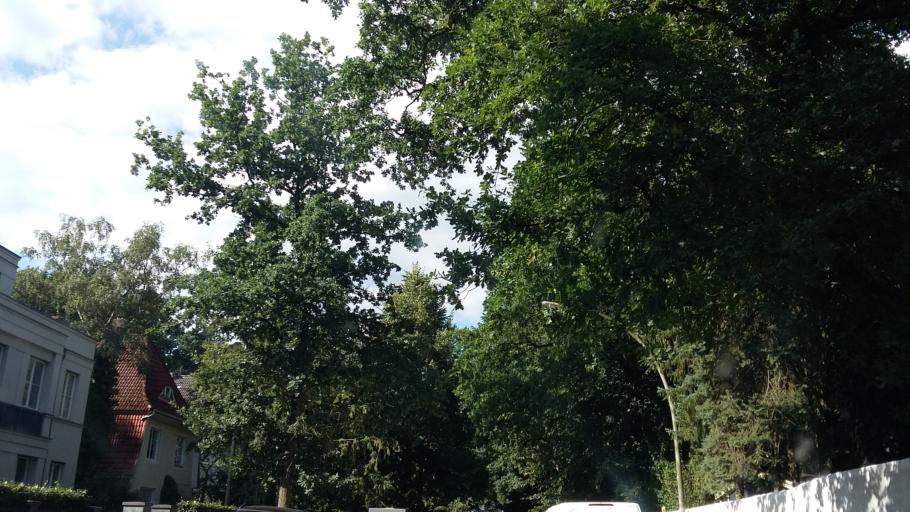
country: DE
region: Hamburg
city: Altona
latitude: 53.5494
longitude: 9.8924
